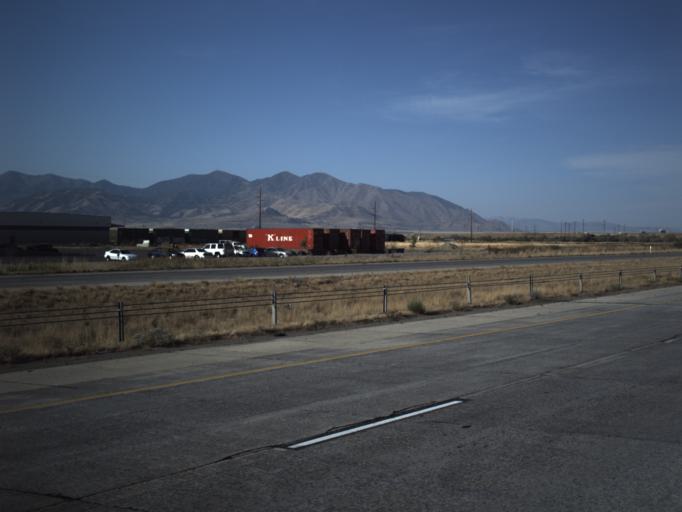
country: US
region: Utah
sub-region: Salt Lake County
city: West Valley City
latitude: 40.7710
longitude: -112.0118
